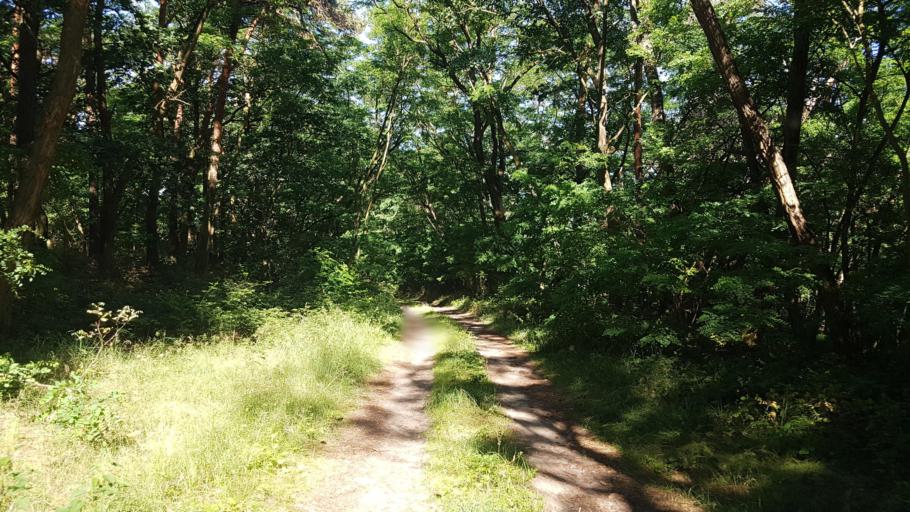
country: DE
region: Brandenburg
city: Juterbog
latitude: 51.9820
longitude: 13.1215
